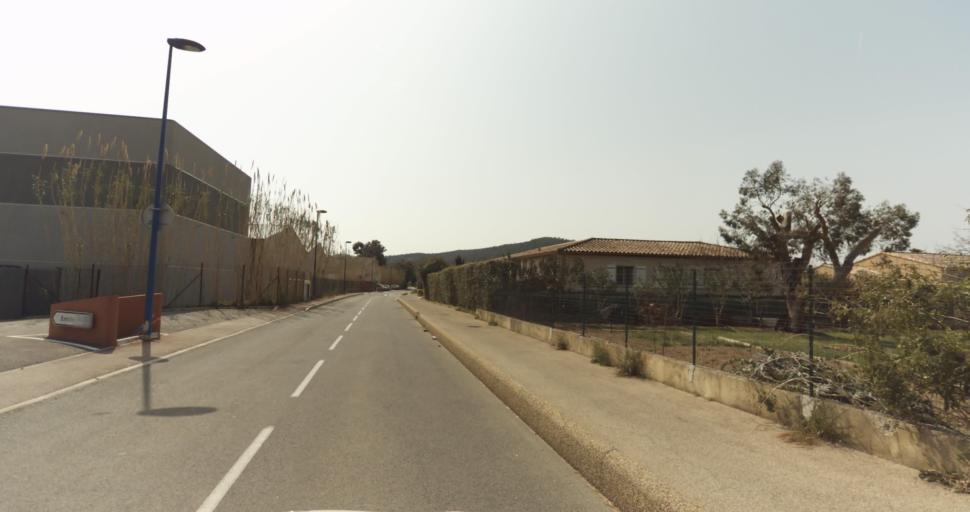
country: FR
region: Provence-Alpes-Cote d'Azur
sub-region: Departement du Var
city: Bormes-les-Mimosas
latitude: 43.1343
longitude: 6.3466
